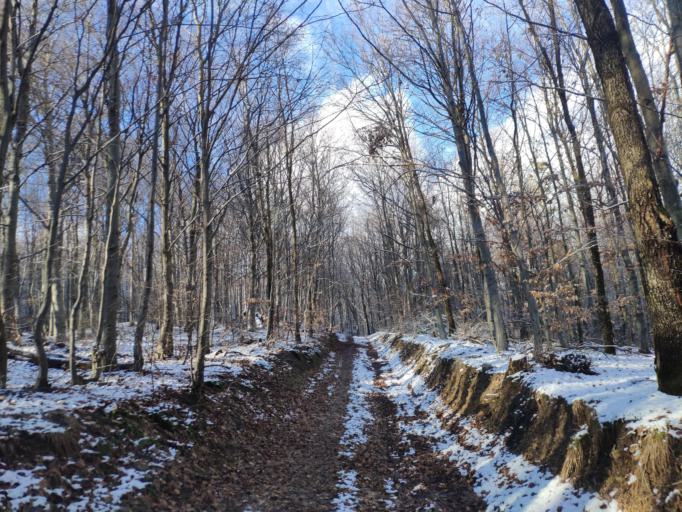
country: SK
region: Kosicky
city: Moldava nad Bodvou
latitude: 48.7388
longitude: 21.1000
